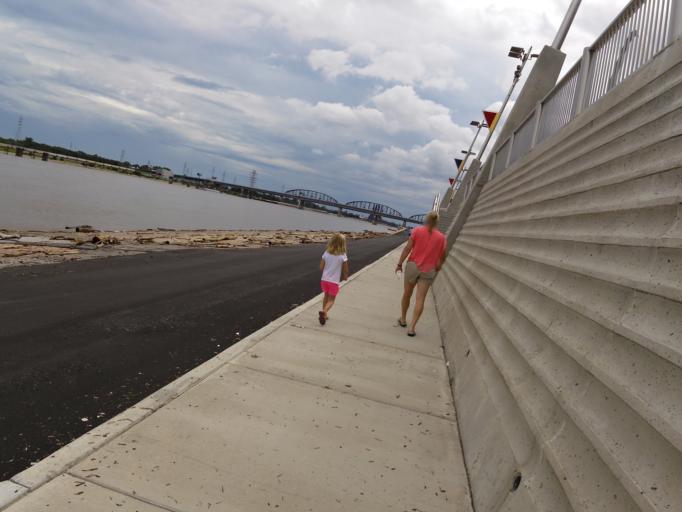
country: US
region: Missouri
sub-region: City of Saint Louis
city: St. Louis
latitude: 38.6281
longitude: -90.1824
